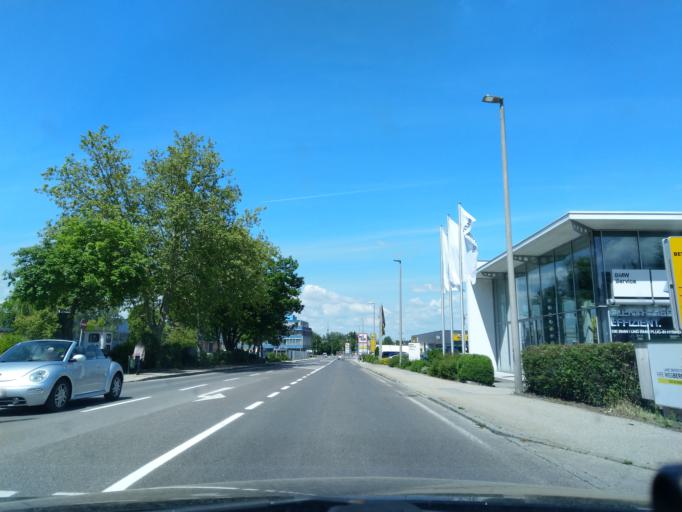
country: AT
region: Upper Austria
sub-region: Politischer Bezirk Ried im Innkreis
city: Ried im Innkreis
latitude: 48.2151
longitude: 13.4822
